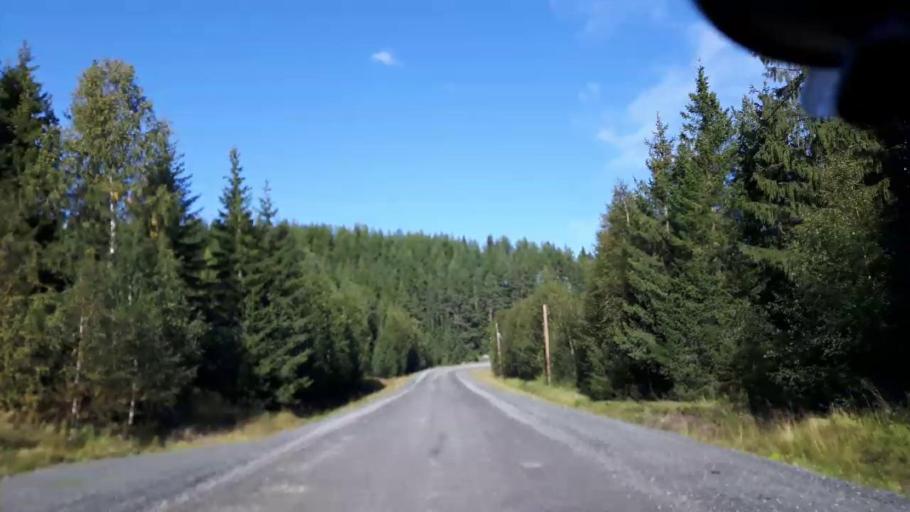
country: SE
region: Vaesternorrland
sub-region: Solleftea Kommun
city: As
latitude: 63.4580
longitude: 16.2500
